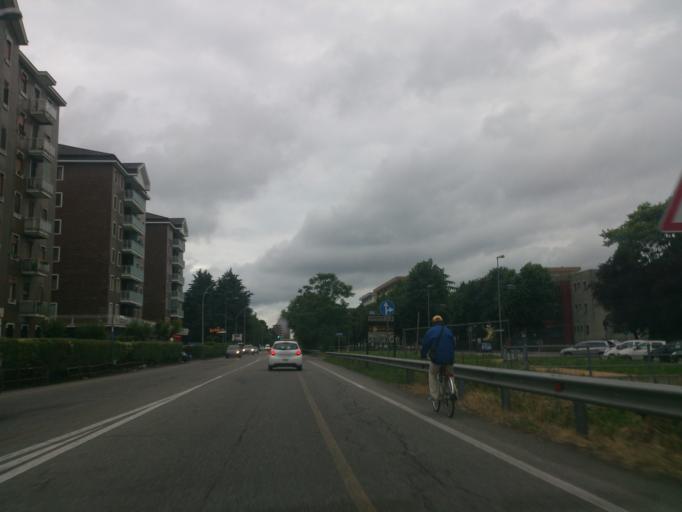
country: IT
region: Lombardy
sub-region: Citta metropolitana di Milano
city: Civesio
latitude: 45.4014
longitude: 9.2770
